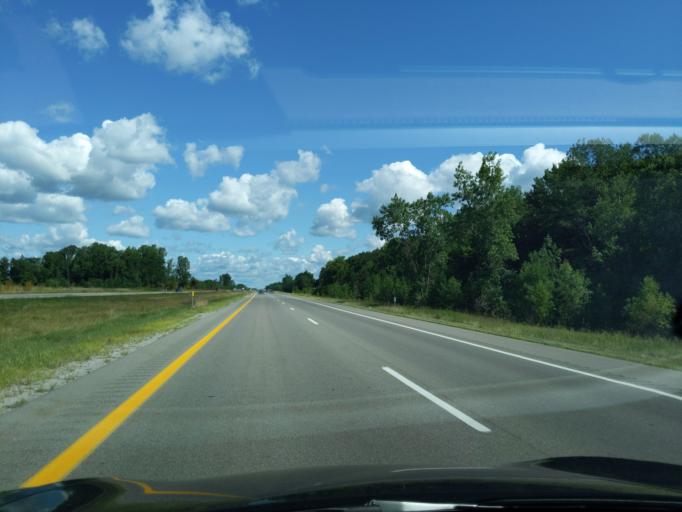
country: US
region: Michigan
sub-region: Isabella County
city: Shepherd
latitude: 43.4584
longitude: -84.6774
